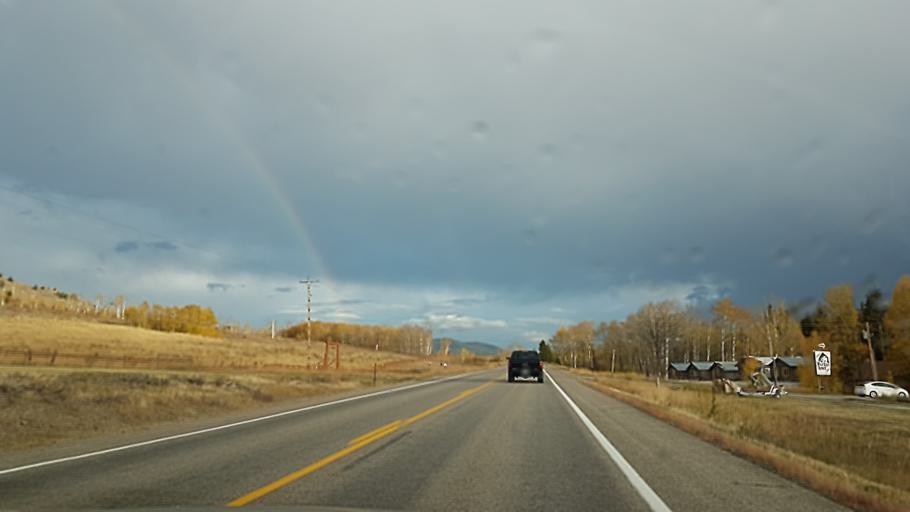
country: US
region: Montana
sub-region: Gallatin County
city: West Yellowstone
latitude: 44.6698
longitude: -111.4007
